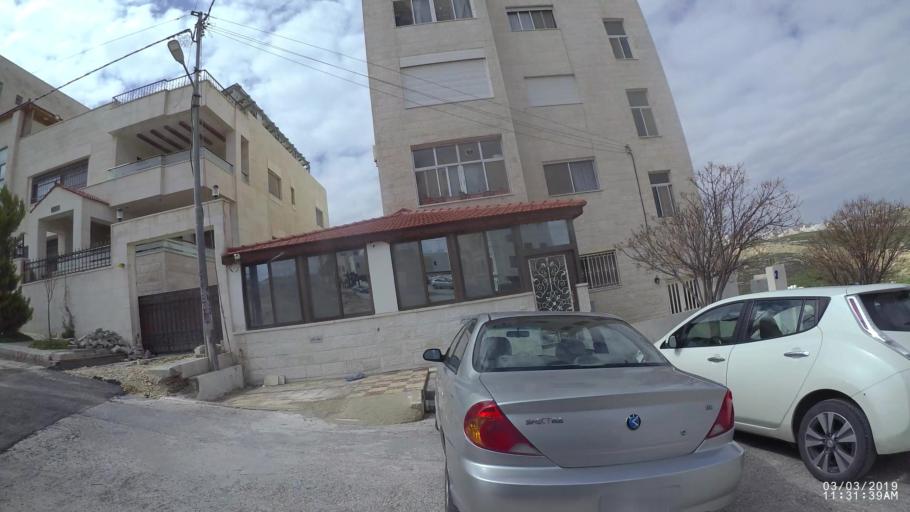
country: JO
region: Amman
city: Al Jubayhah
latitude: 32.0054
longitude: 35.9128
